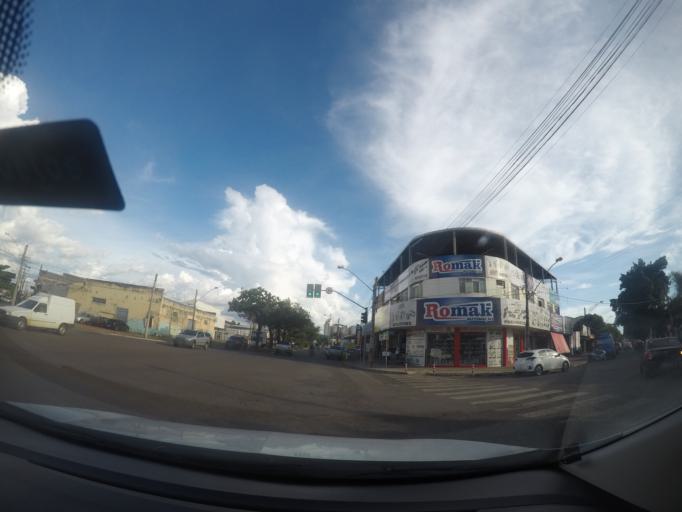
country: BR
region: Goias
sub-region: Goiania
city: Goiania
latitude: -16.6697
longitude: -49.3063
